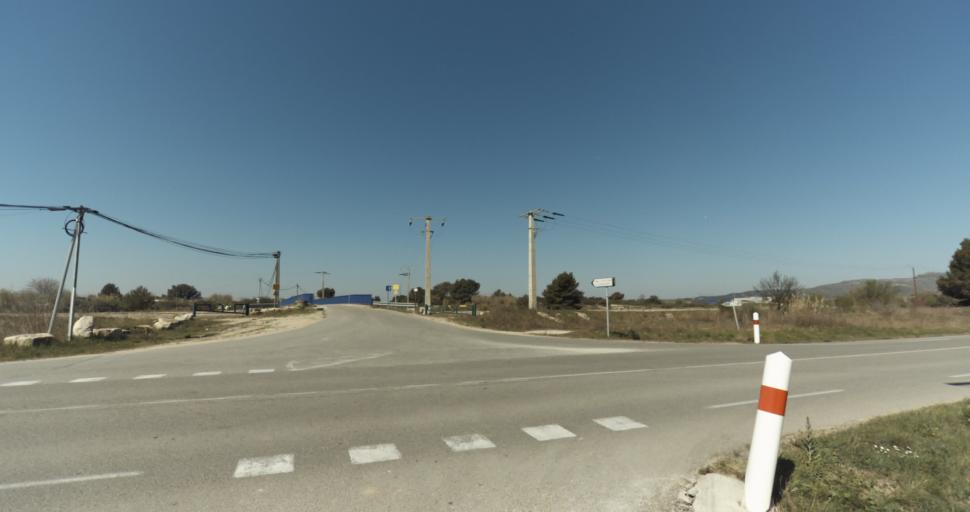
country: FR
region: Provence-Alpes-Cote d'Azur
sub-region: Departement des Bouches-du-Rhone
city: Lancon-Provence
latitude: 43.6135
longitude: 5.1388
